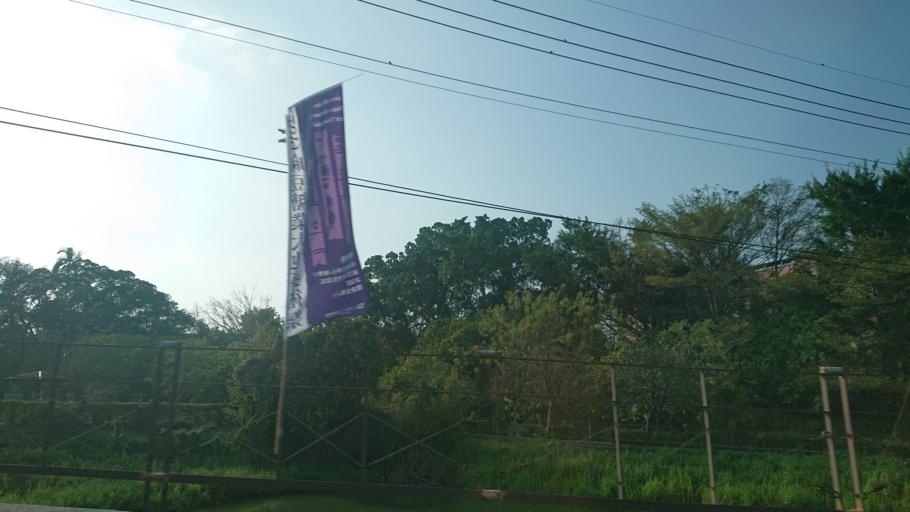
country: TW
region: Taiwan
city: Xinying
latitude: 23.1903
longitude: 120.2714
